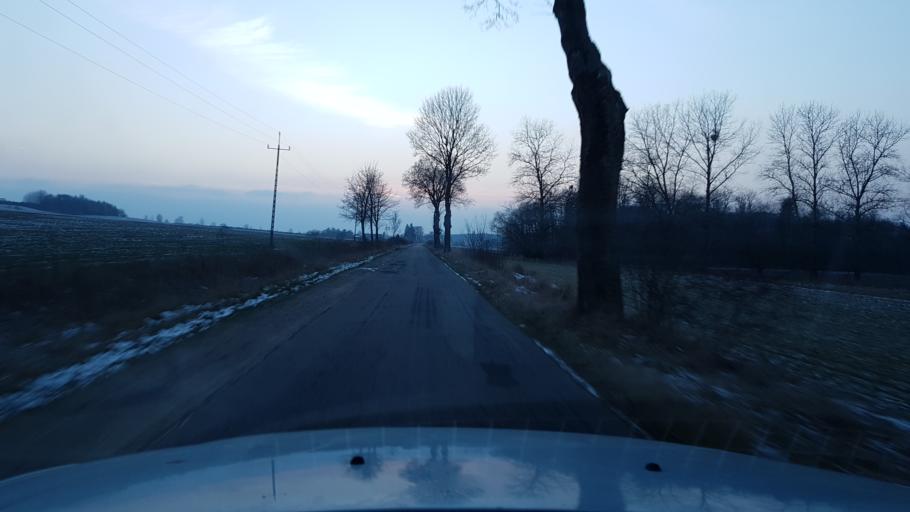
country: PL
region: West Pomeranian Voivodeship
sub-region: Powiat bialogardzki
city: Karlino
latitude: 53.9893
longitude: 15.8128
